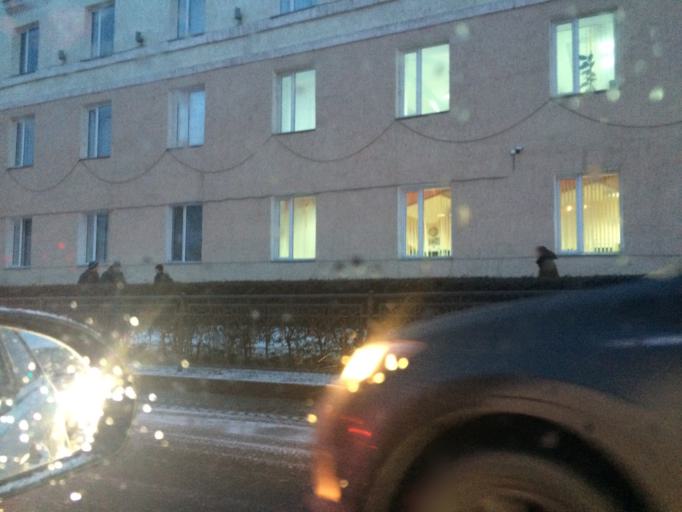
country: KZ
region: Astana Qalasy
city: Astana
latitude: 51.1784
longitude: 71.4179
